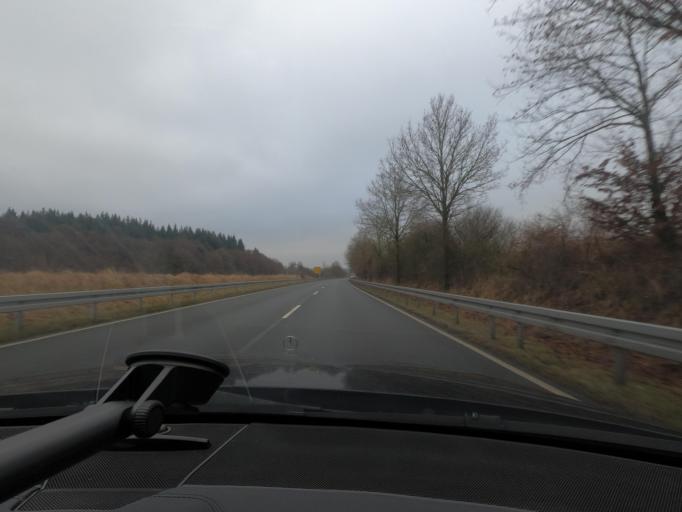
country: DE
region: Hesse
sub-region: Regierungsbezirk Kassel
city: Bad Arolsen
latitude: 51.4410
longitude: 9.0196
